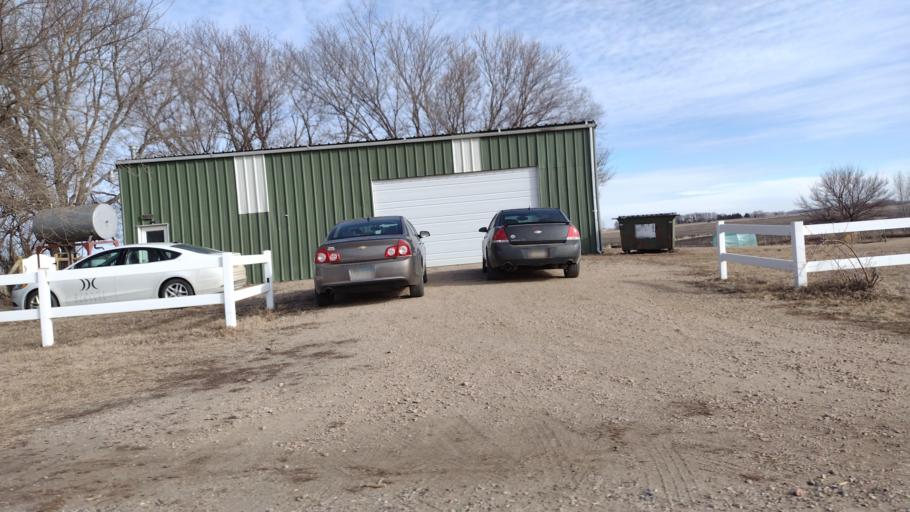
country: US
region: South Dakota
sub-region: Union County
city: Beresford
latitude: 42.9607
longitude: -96.8055
